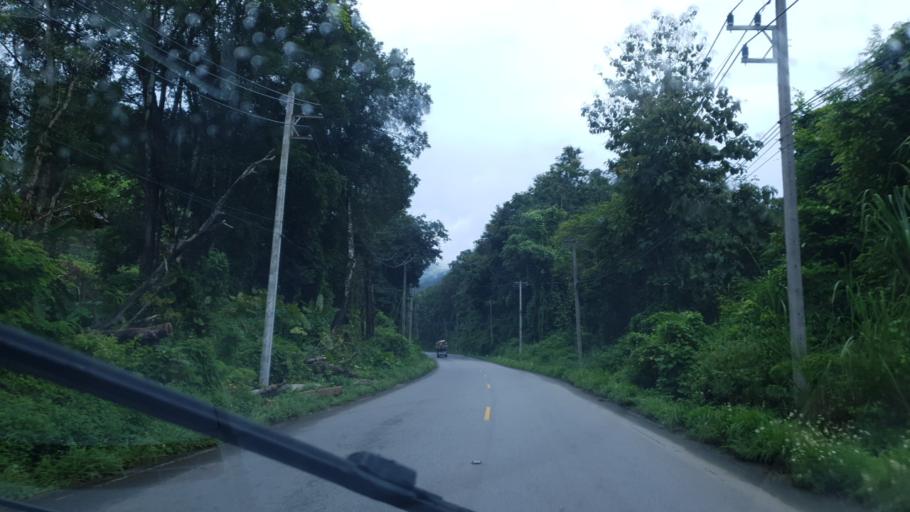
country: TH
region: Mae Hong Son
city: Ban Huai I Huak
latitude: 18.1528
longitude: 97.9680
